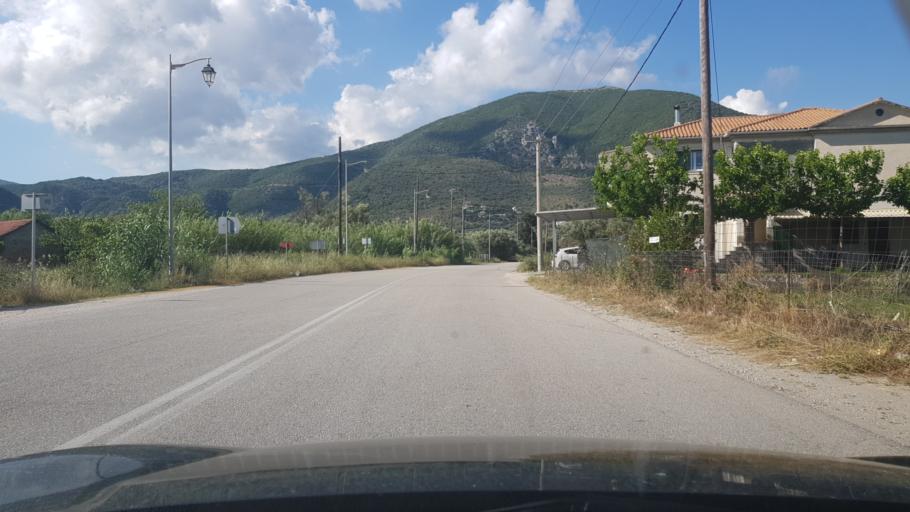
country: GR
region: Ionian Islands
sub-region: Lefkada
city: Nidri
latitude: 38.7056
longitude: 20.7038
